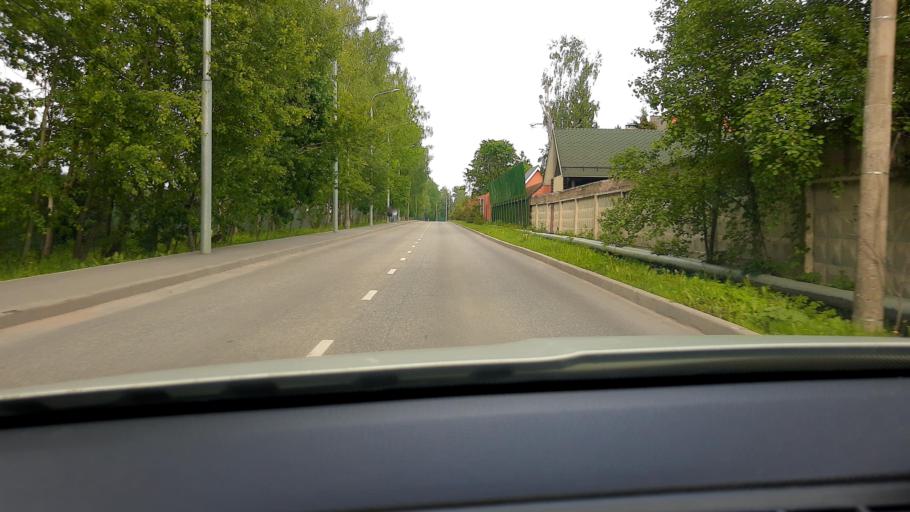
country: RU
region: Moskovskaya
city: Vatutinki
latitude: 55.5095
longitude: 37.3743
